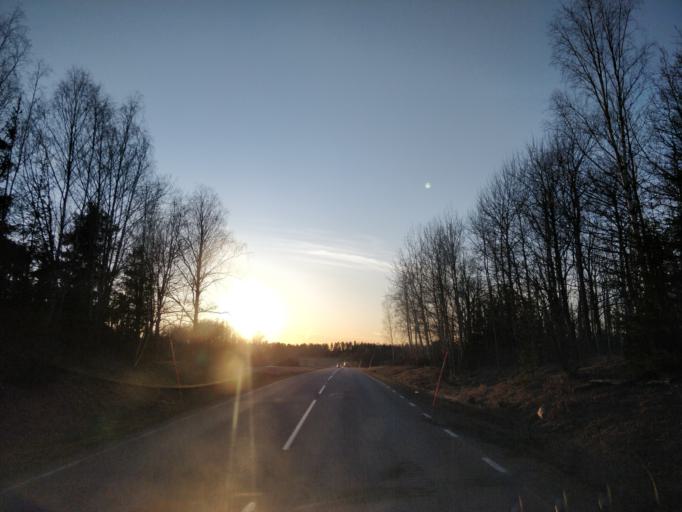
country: SE
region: Uppsala
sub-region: Enkopings Kommun
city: Orsundsbro
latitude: 59.7487
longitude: 17.2614
